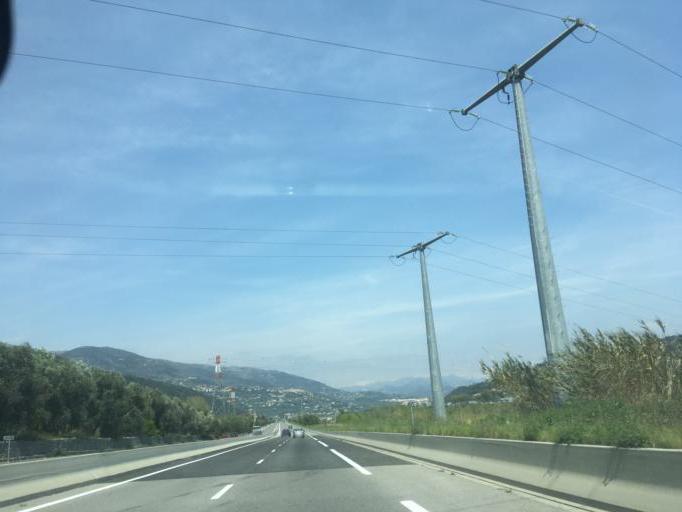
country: FR
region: Provence-Alpes-Cote d'Azur
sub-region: Departement des Alpes-Maritimes
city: La Gaude
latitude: 43.7160
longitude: 7.1828
